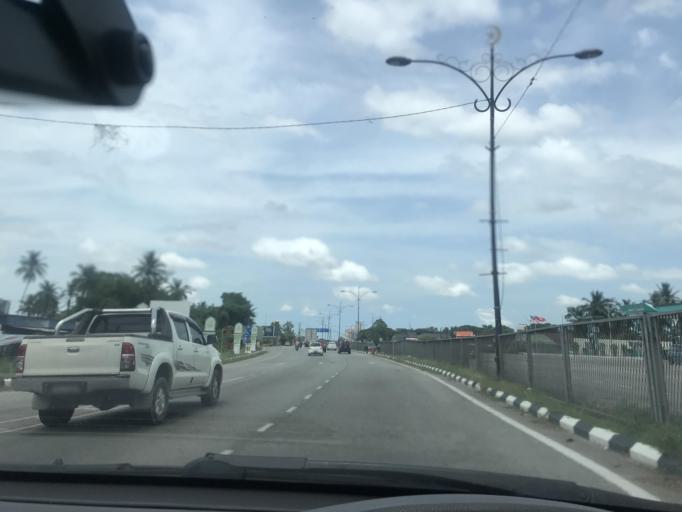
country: MY
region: Kelantan
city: Kota Bharu
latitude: 6.1173
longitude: 102.2225
